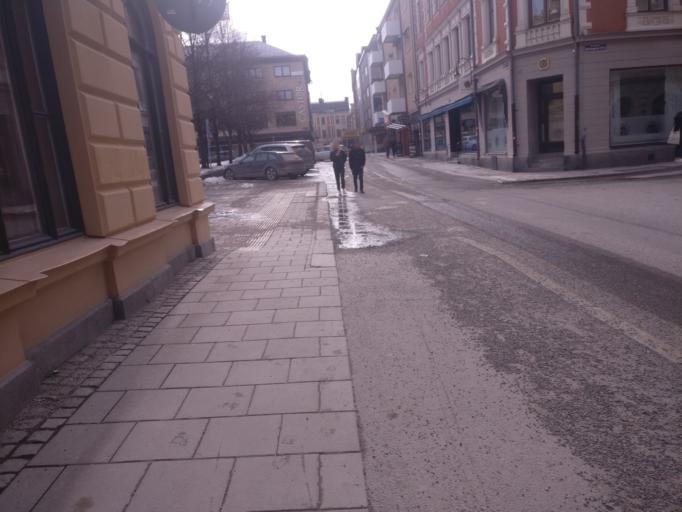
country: SE
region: Vaesternorrland
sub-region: Sundsvalls Kommun
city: Sundsvall
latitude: 62.3902
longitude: 17.3058
